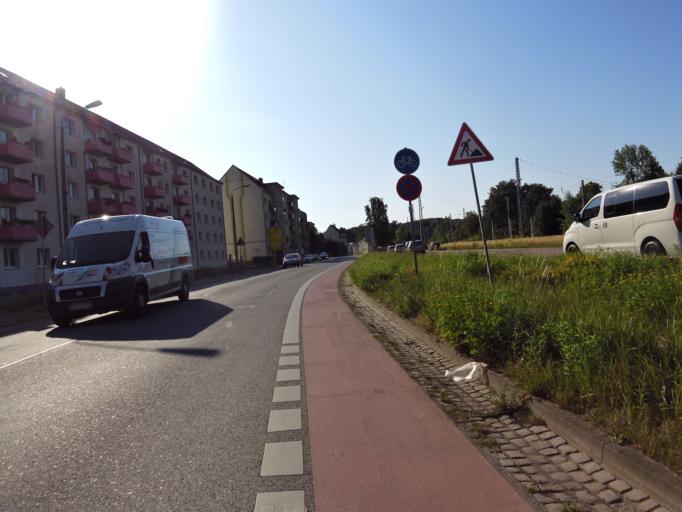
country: DE
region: Saxony
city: Dobeln
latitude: 51.1251
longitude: 13.1010
